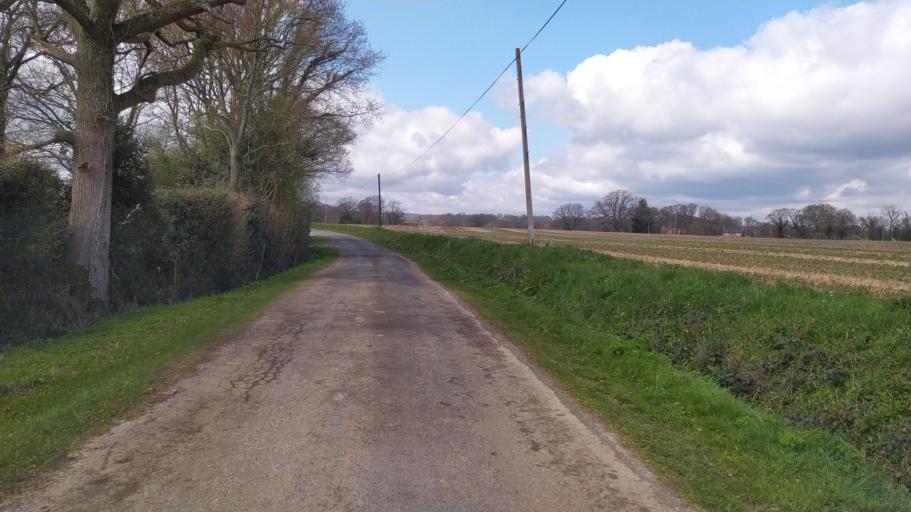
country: GB
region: England
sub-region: West Sussex
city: Petworth
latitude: 51.0255
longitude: -0.5825
